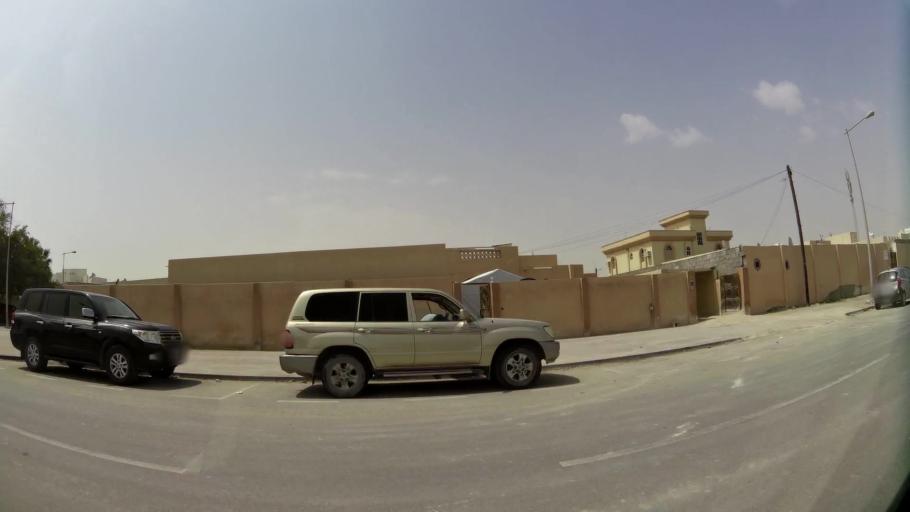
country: QA
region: Baladiyat ar Rayyan
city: Ar Rayyan
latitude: 25.2433
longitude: 51.4307
